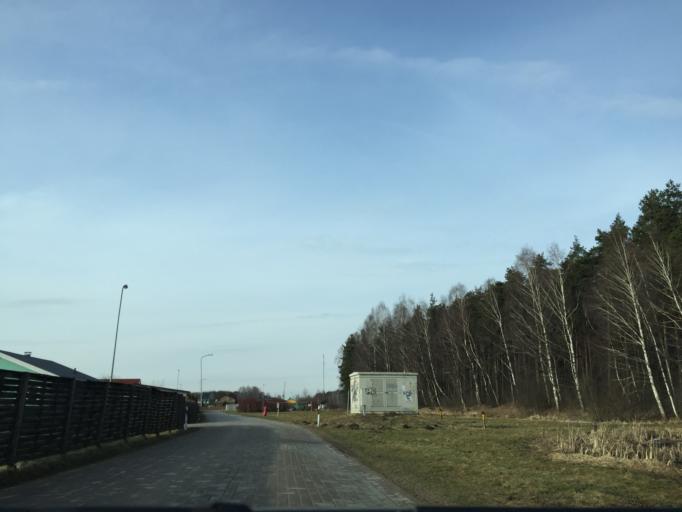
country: LV
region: Stopini
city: Ulbroka
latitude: 56.9282
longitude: 24.2647
